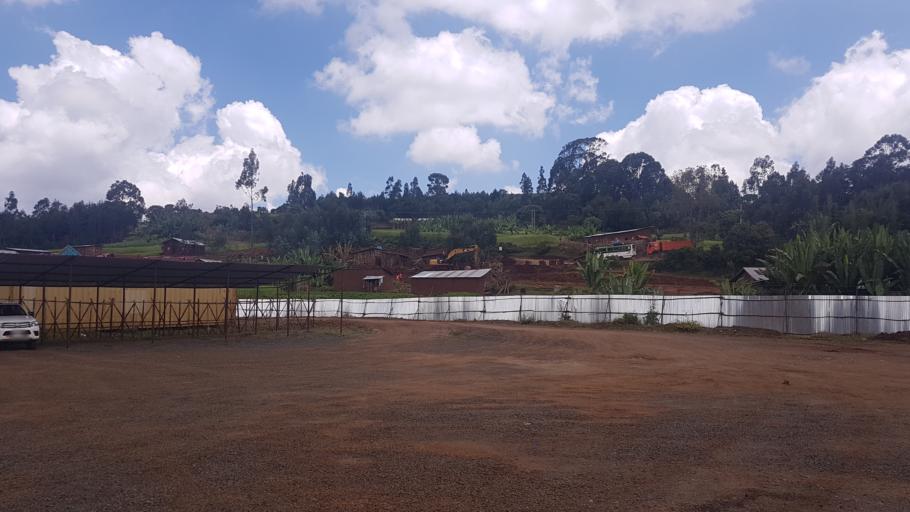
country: ET
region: Southern Nations, Nationalities, and People's Region
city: Arba Minch'
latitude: 6.3217
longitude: 37.5351
